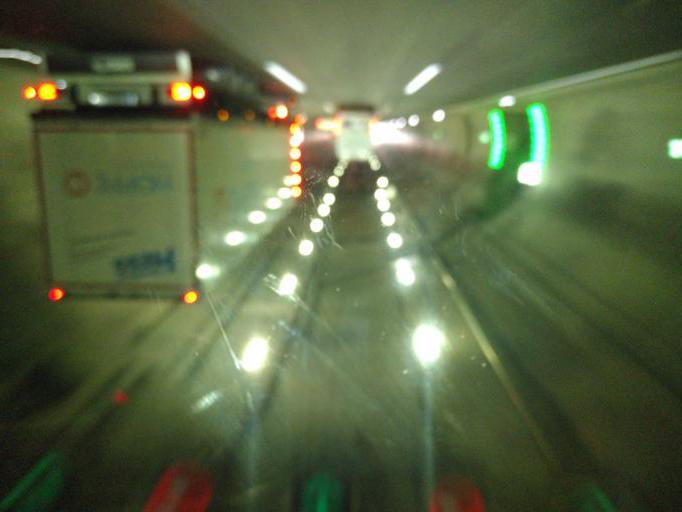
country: DE
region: Thuringia
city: Rothenstein
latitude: 50.8737
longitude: 11.5707
